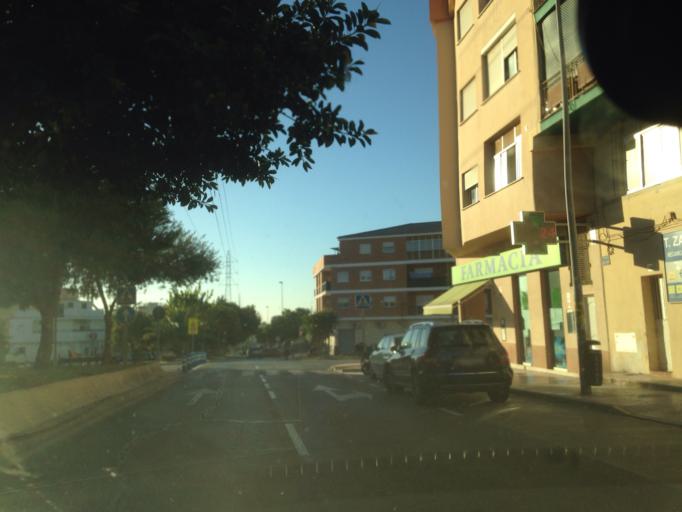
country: ES
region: Andalusia
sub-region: Provincia de Malaga
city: Malaga
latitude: 36.7211
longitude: -4.4721
